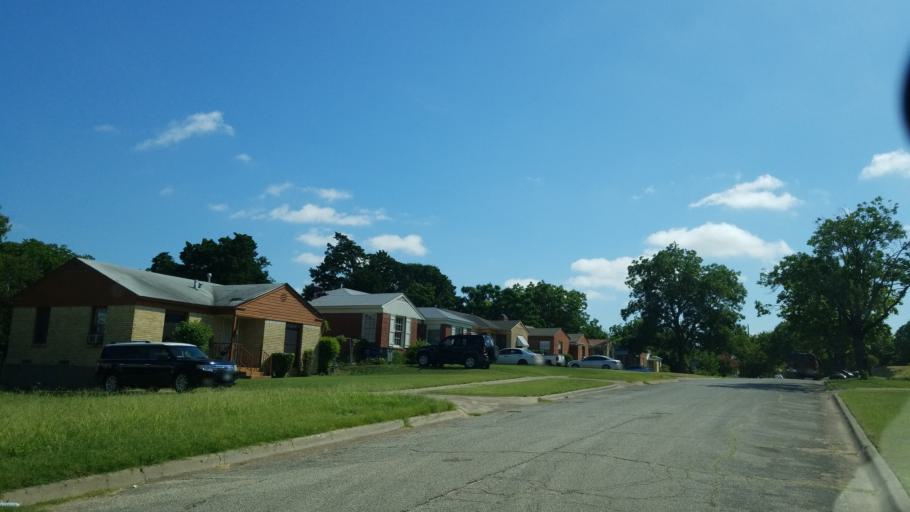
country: US
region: Texas
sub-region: Dallas County
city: Dallas
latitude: 32.7324
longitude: -96.7986
